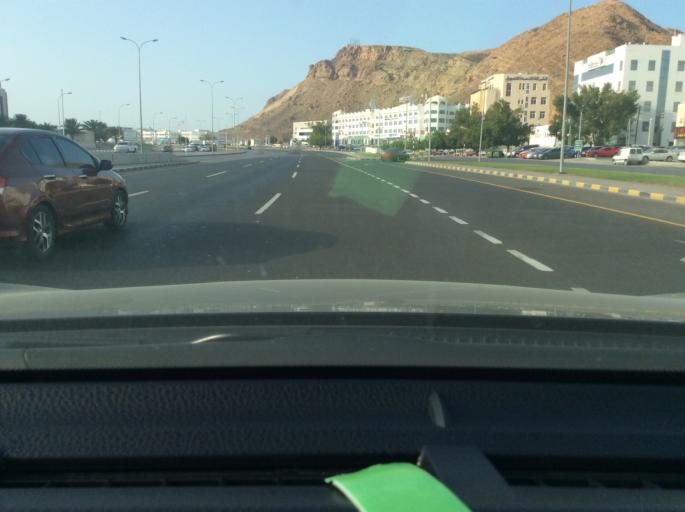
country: OM
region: Muhafazat Masqat
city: Muscat
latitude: 23.5971
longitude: 58.5207
